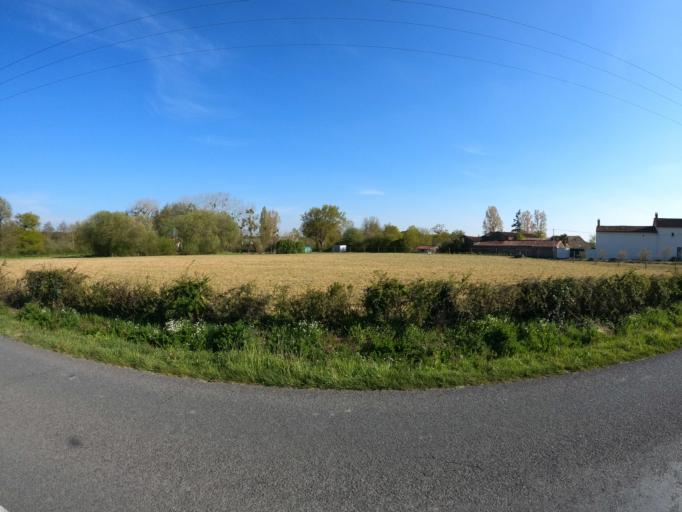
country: FR
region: Pays de la Loire
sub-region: Departement de la Vendee
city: La Gaubretiere
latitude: 46.9348
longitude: -1.0862
